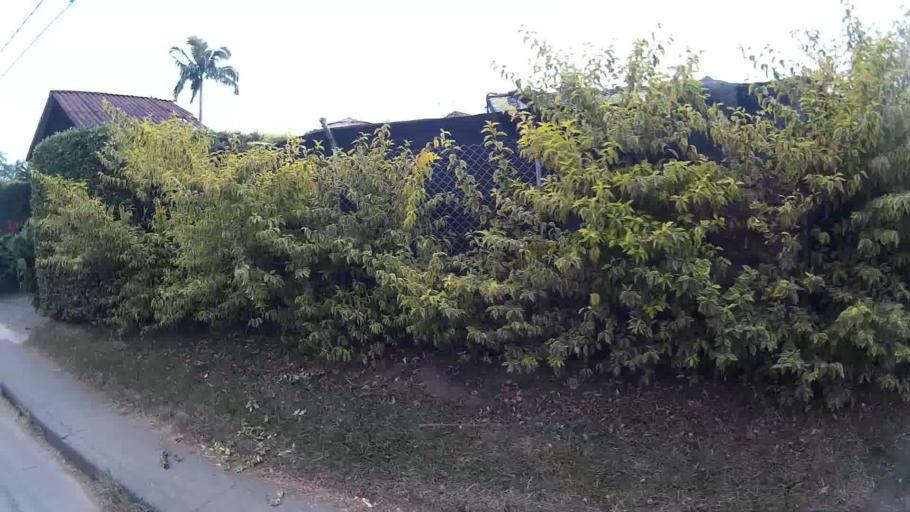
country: CO
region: Risaralda
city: Pereira
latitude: 4.8239
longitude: -75.7567
